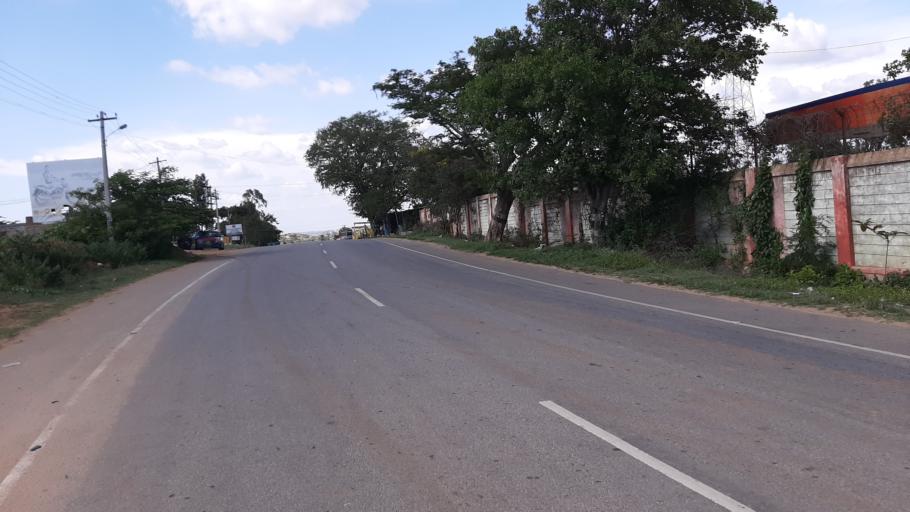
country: IN
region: Tamil Nadu
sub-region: Krishnagiri
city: Denkanikota
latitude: 12.5381
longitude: 77.7888
